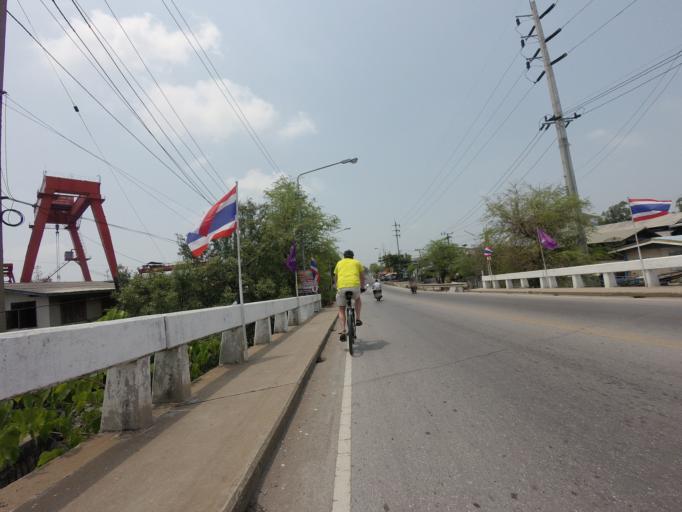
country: TH
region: Samut Prakan
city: Phra Samut Chedi
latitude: 13.5734
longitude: 100.5739
